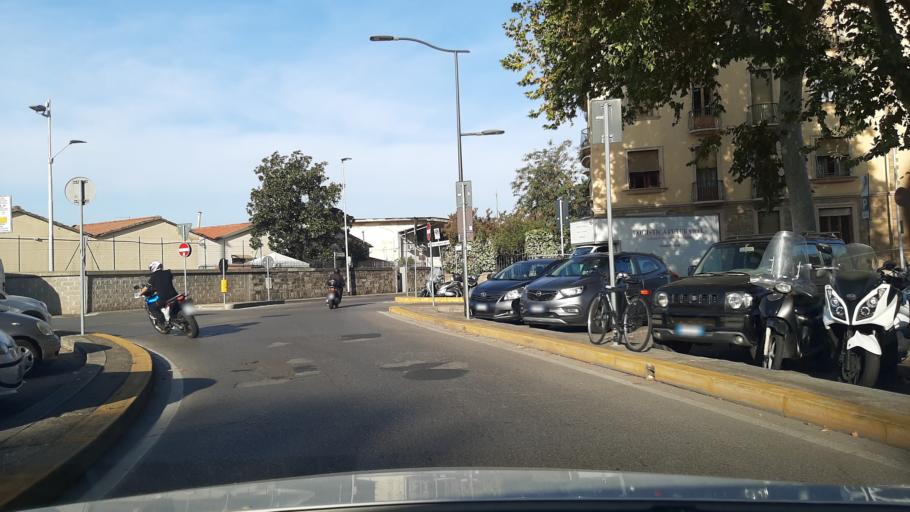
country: IT
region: Tuscany
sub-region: Province of Florence
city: Fiesole
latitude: 43.7781
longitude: 11.2784
